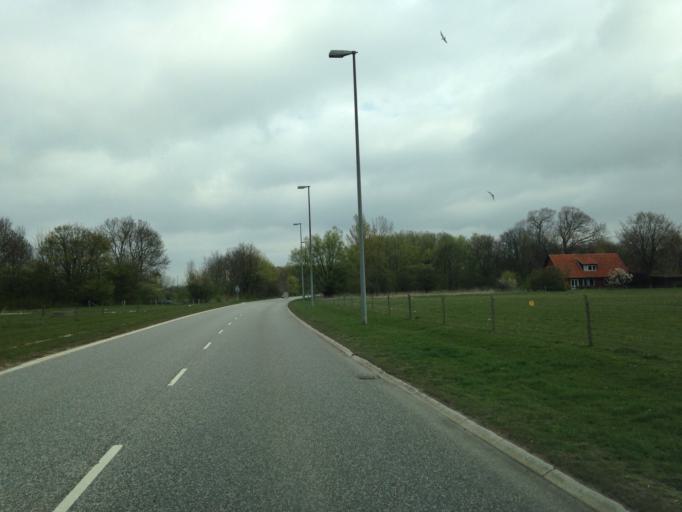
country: DK
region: Capital Region
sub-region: Ishoj Kommune
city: Ishoj
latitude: 55.6064
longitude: 12.3269
